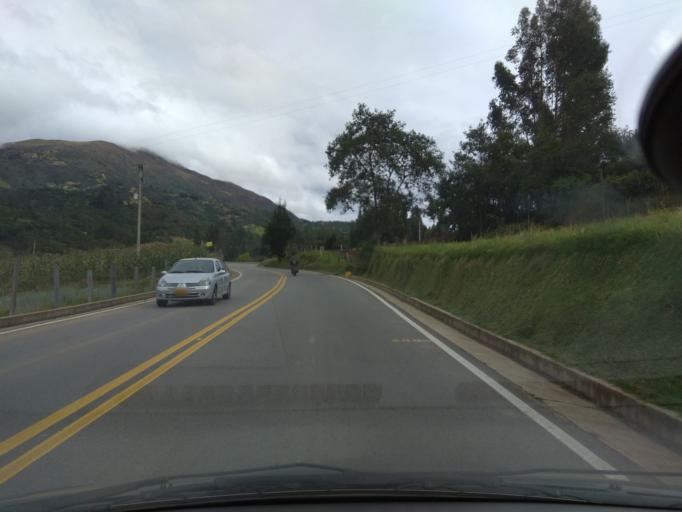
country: CO
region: Boyaca
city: Santa Rosa de Viterbo
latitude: 5.9001
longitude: -72.9757
